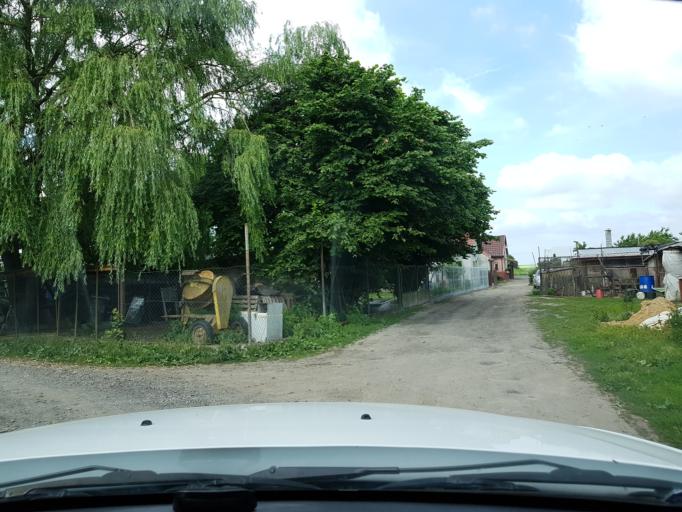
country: PL
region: West Pomeranian Voivodeship
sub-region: Powiat gryfinski
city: Banie
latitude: 53.1264
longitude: 14.5973
